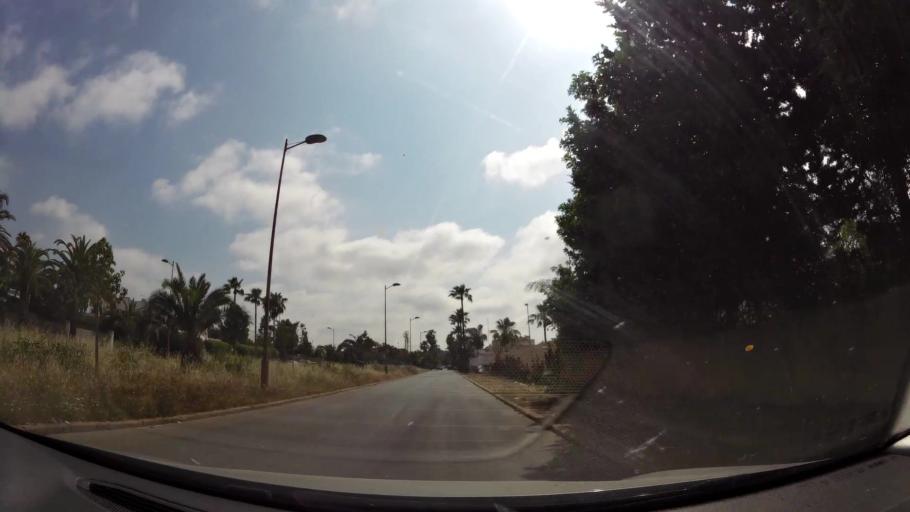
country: MA
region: Rabat-Sale-Zemmour-Zaer
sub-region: Rabat
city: Rabat
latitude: 33.9898
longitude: -6.8303
